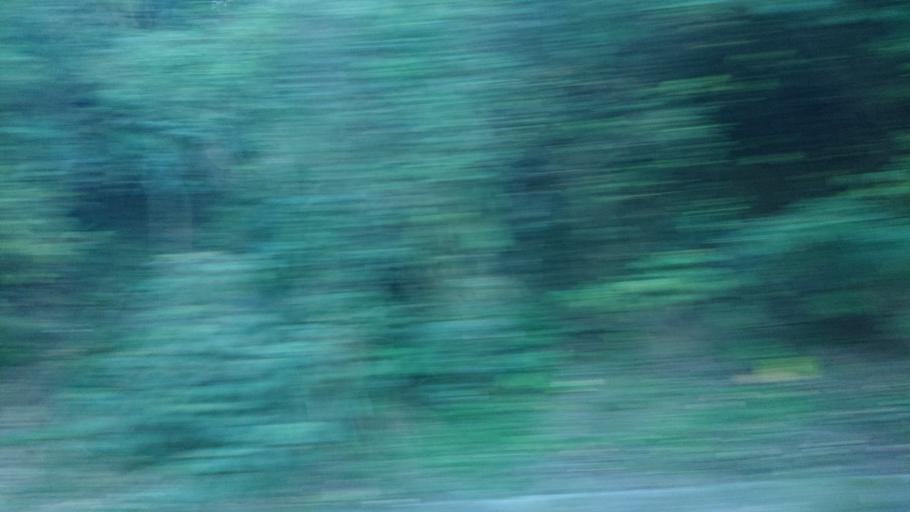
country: TW
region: Taiwan
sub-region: Chiayi
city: Jiayi Shi
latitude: 23.5188
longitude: 120.6269
